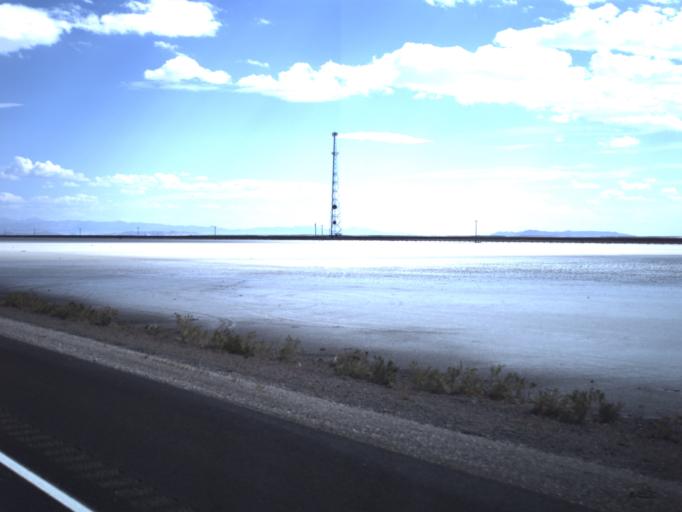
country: US
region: Utah
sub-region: Tooele County
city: Wendover
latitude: 40.7324
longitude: -113.5666
